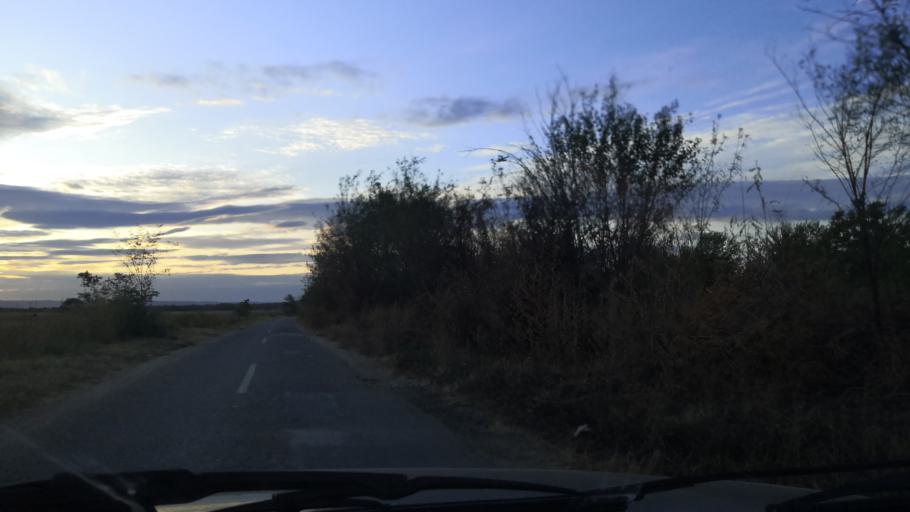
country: RO
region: Mehedinti
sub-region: Comuna Gruia
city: Izvoarele
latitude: 44.2763
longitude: 22.6580
